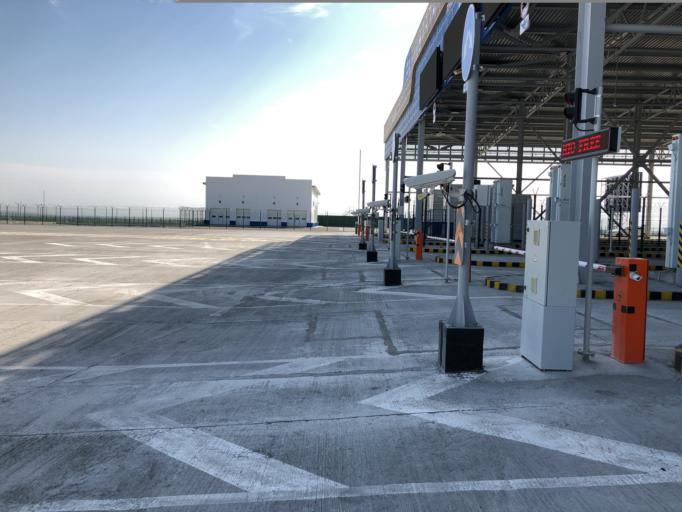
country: KZ
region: Almaty Oblysy
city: Zharkent
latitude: 44.1575
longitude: 80.3991
